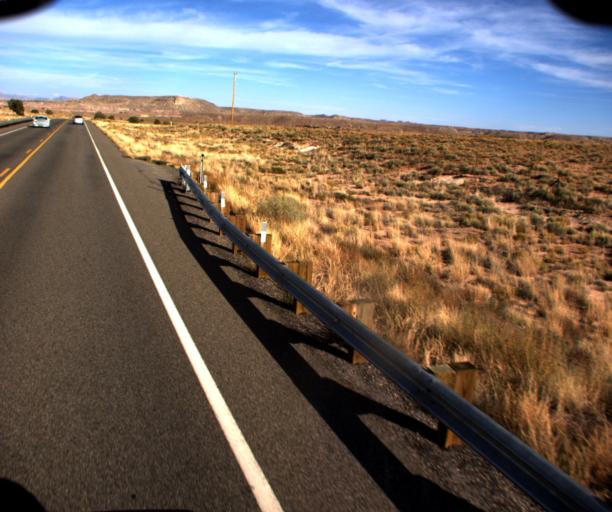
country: US
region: New Mexico
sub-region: San Juan County
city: Shiprock
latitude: 36.9316
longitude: -109.1463
